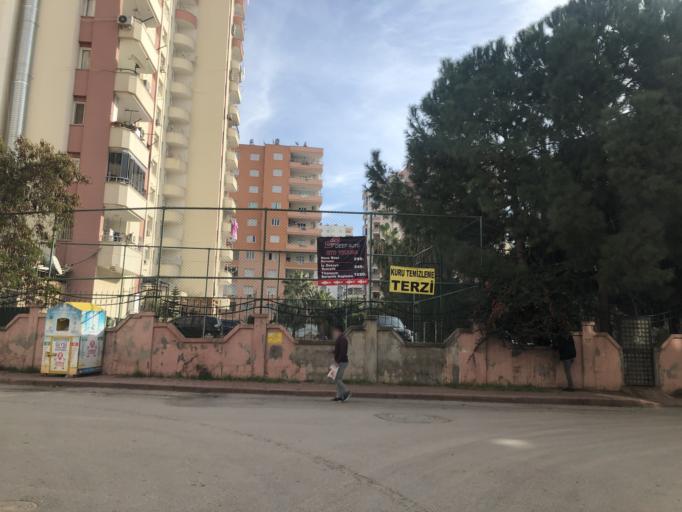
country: TR
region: Adana
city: Adana
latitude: 37.0516
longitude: 35.2927
